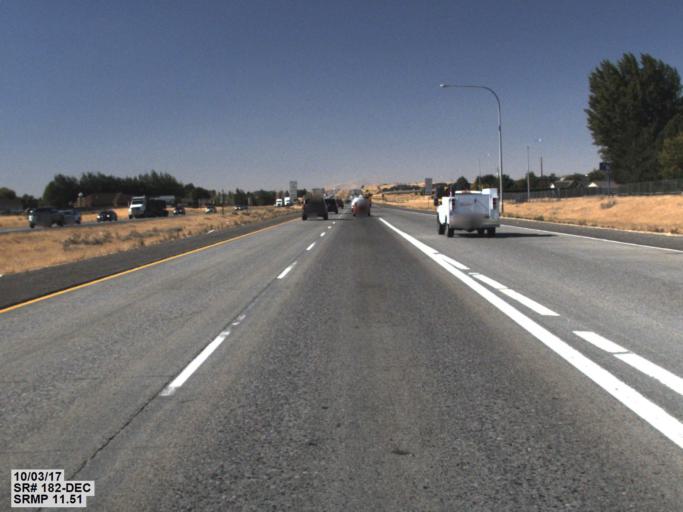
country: US
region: Washington
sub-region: Benton County
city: Kennewick
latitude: 46.2530
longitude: -119.1408
